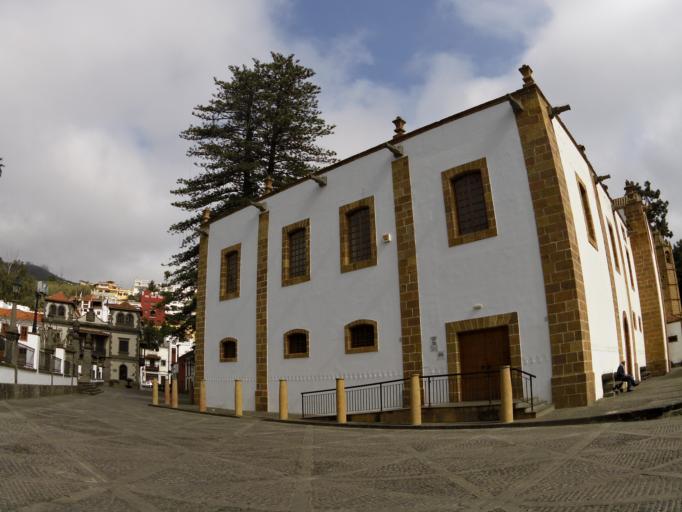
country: ES
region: Canary Islands
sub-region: Provincia de Las Palmas
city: Teror
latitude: 28.0589
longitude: -15.5480
